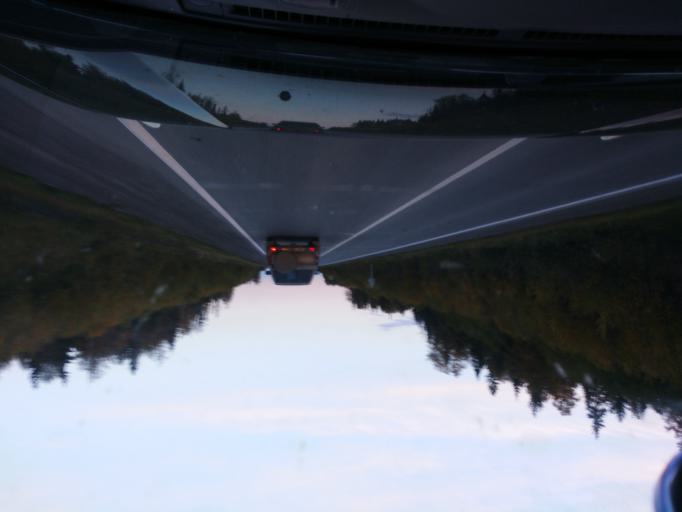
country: RU
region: Perm
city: Sylva
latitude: 58.2875
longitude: 56.7425
